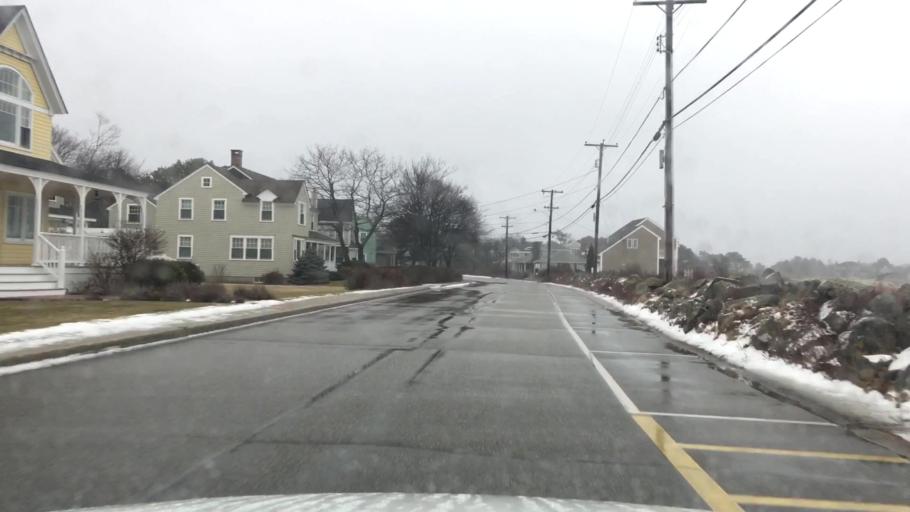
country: US
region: Maine
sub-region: York County
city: Arundel
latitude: 43.4006
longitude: -70.4089
